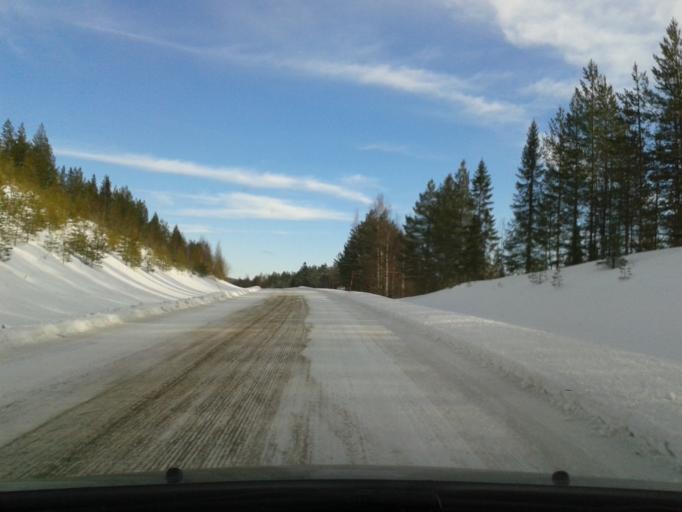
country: SE
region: Vaesterbotten
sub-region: Asele Kommun
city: Asele
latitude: 64.3170
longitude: 17.1299
